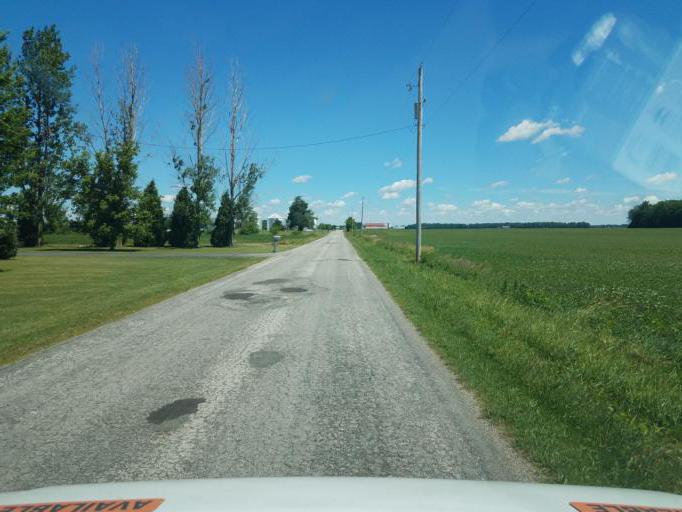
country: US
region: Ohio
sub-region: Morrow County
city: Cardington
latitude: 40.5805
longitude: -82.9381
